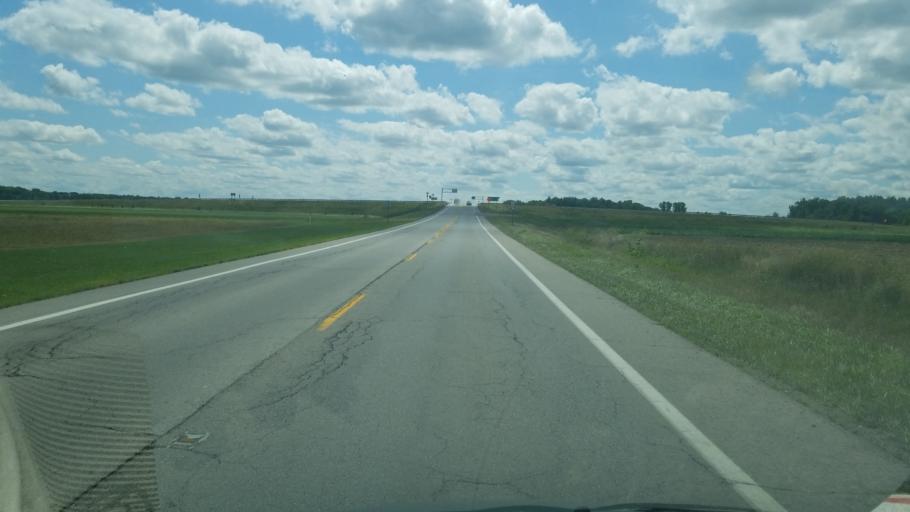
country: US
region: Ohio
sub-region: Henry County
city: Liberty Center
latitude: 41.4327
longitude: -84.0087
